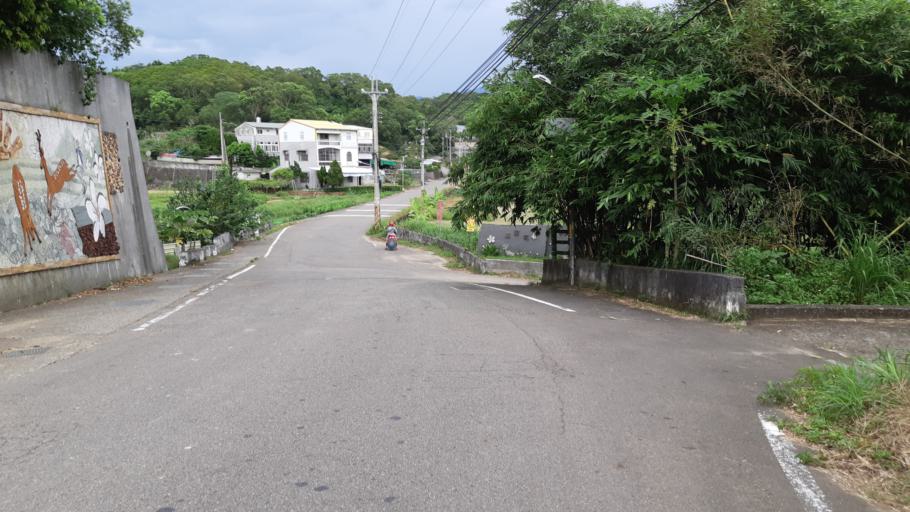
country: TW
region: Taiwan
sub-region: Miaoli
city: Miaoli
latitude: 24.6567
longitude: 120.8914
